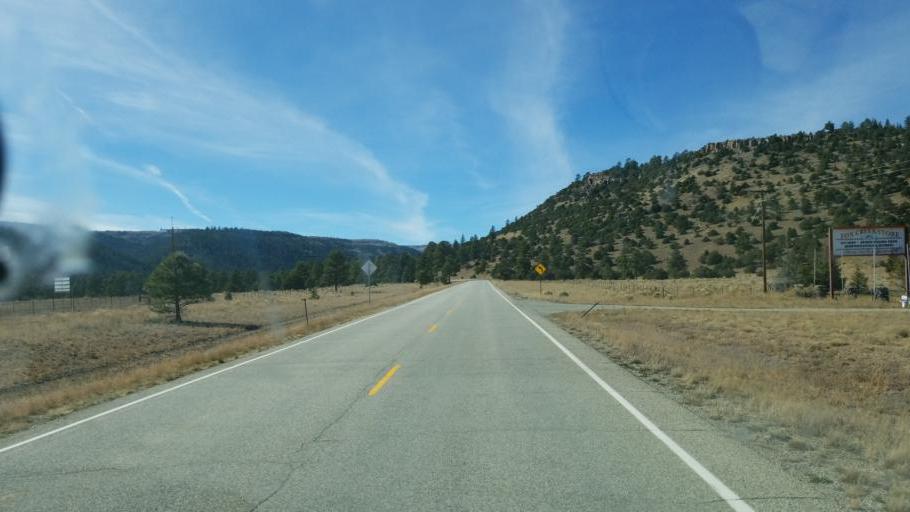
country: US
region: Colorado
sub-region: Conejos County
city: Conejos
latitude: 37.0681
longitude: -106.2233
